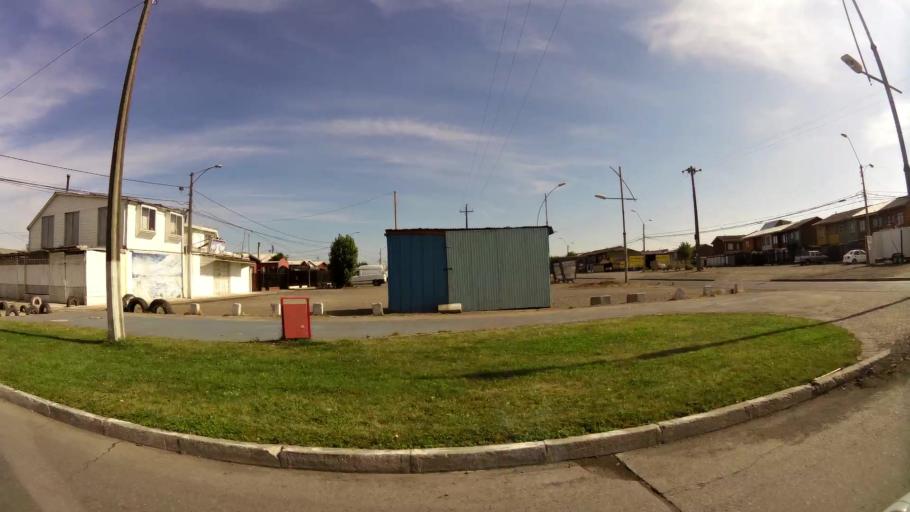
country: CL
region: Biobio
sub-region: Provincia de Concepcion
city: Talcahuano
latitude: -36.7867
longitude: -73.1103
